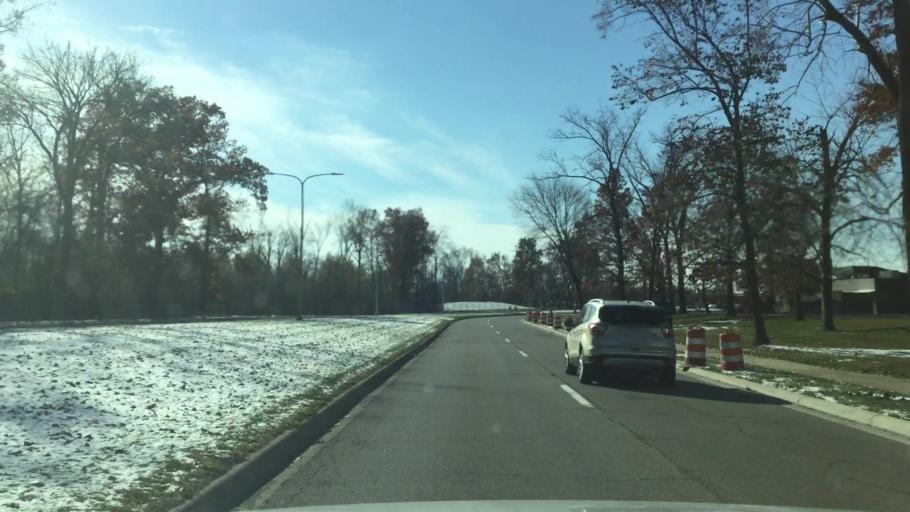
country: US
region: Michigan
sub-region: Macomb County
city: Center Line
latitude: 42.5227
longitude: -83.0448
